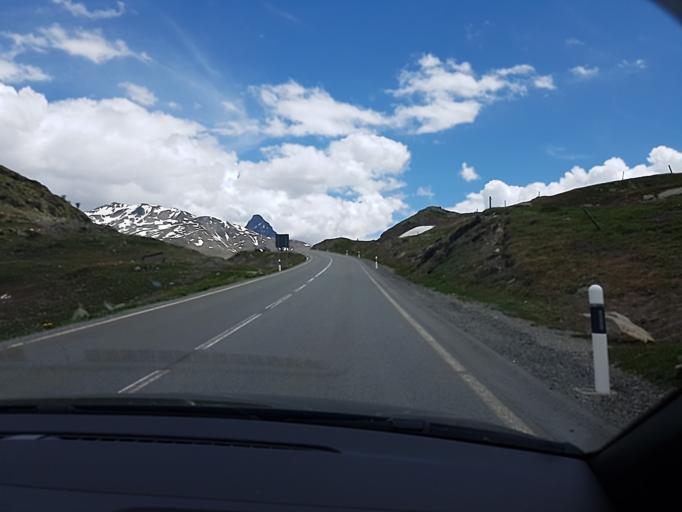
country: CH
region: Grisons
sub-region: Bernina District
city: Poschiavo
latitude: 46.4107
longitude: 10.0241
